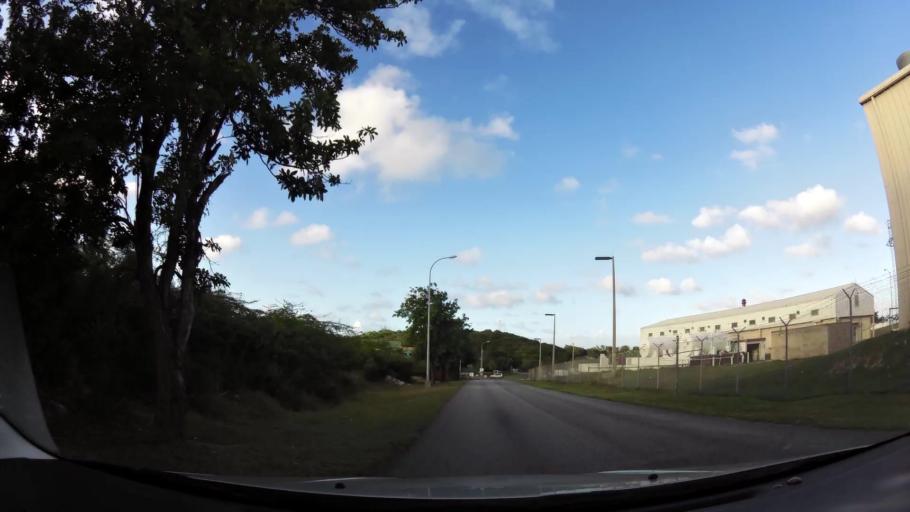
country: AG
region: Saint George
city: Piggotts
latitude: 17.1503
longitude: -61.7945
